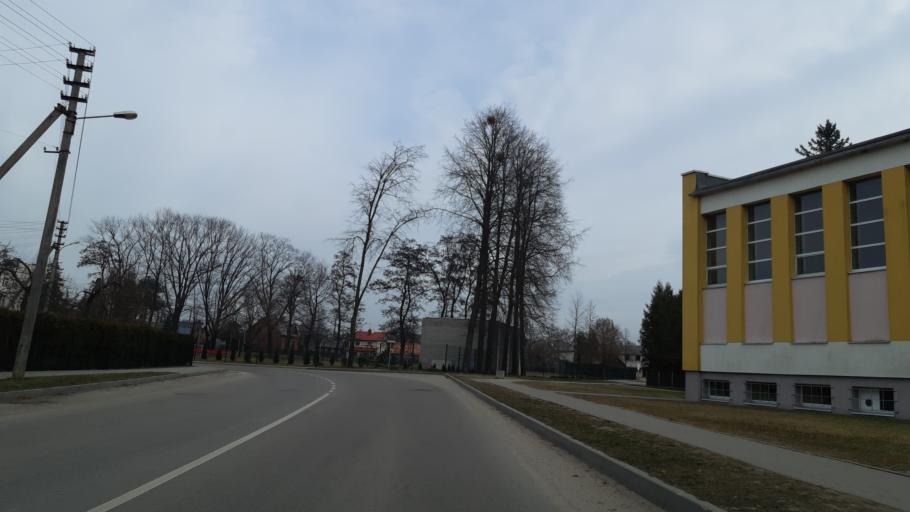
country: LT
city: Kazlu Ruda
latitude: 54.7523
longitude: 23.4951
